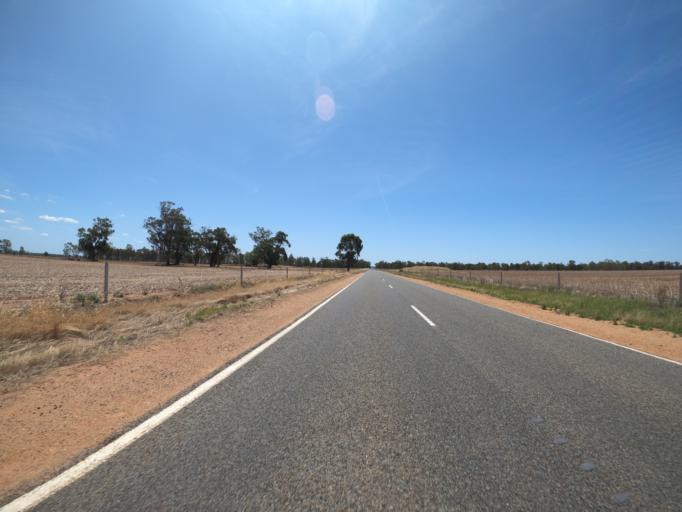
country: AU
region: Victoria
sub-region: Moira
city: Yarrawonga
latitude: -36.1653
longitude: 145.9672
